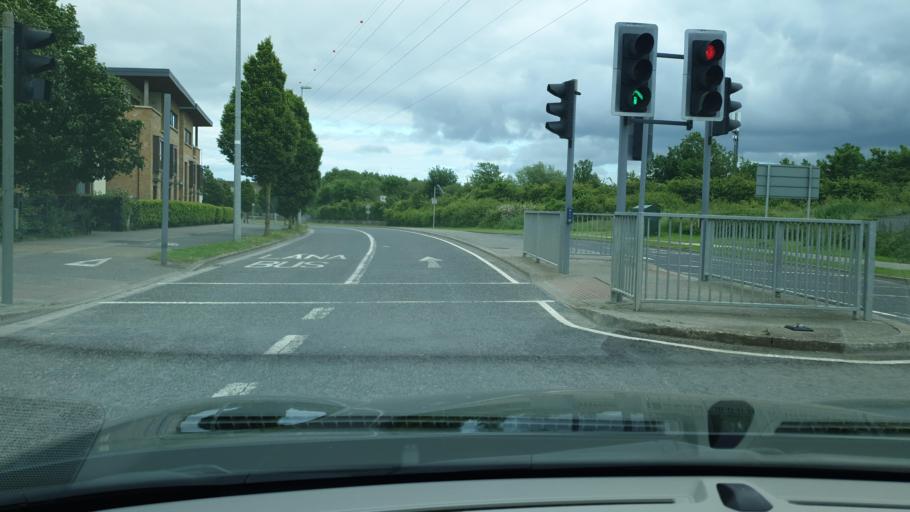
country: IE
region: Leinster
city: Lucan
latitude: 53.3362
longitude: -6.4571
